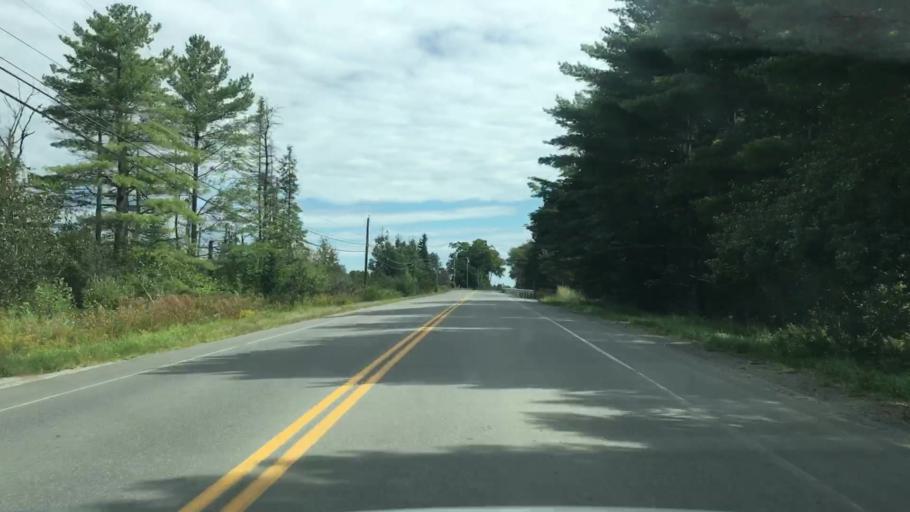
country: US
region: Maine
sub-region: Piscataquis County
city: Dover-Foxcroft
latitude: 45.2011
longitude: -69.1957
